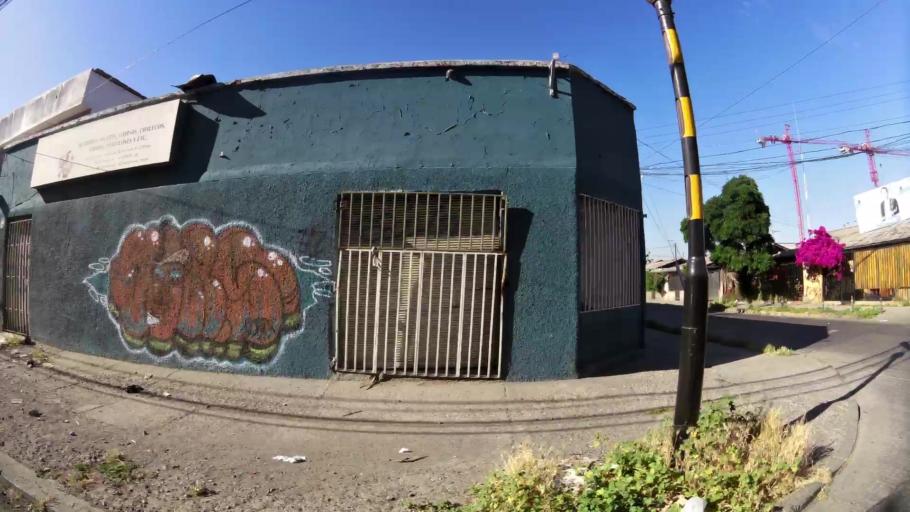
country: CL
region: Santiago Metropolitan
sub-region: Provincia de Maipo
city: San Bernardo
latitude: -33.5395
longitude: -70.6806
